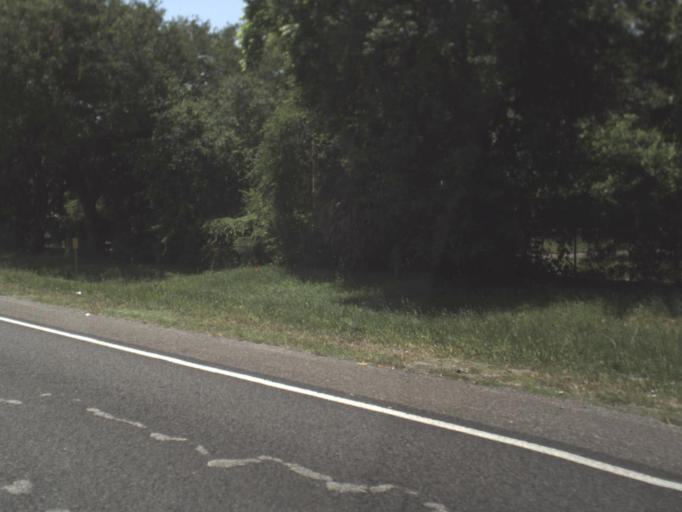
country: US
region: Florida
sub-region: Duval County
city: Jacksonville
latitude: 30.3607
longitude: -81.6688
